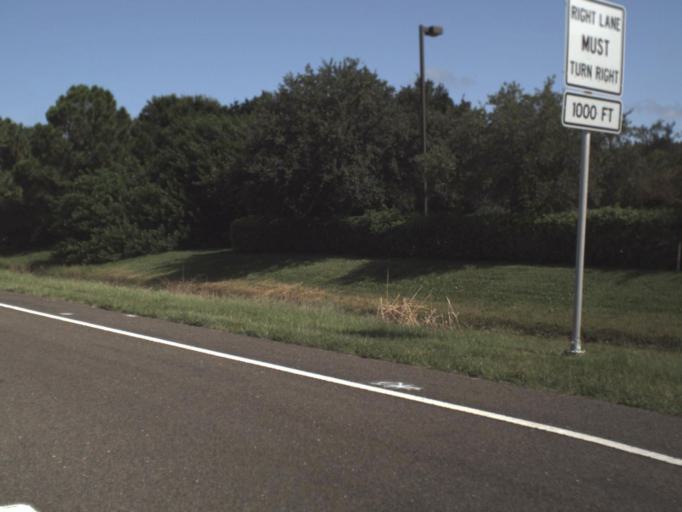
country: US
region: Florida
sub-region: Pinellas County
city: Feather Sound
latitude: 27.8845
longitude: -82.6662
